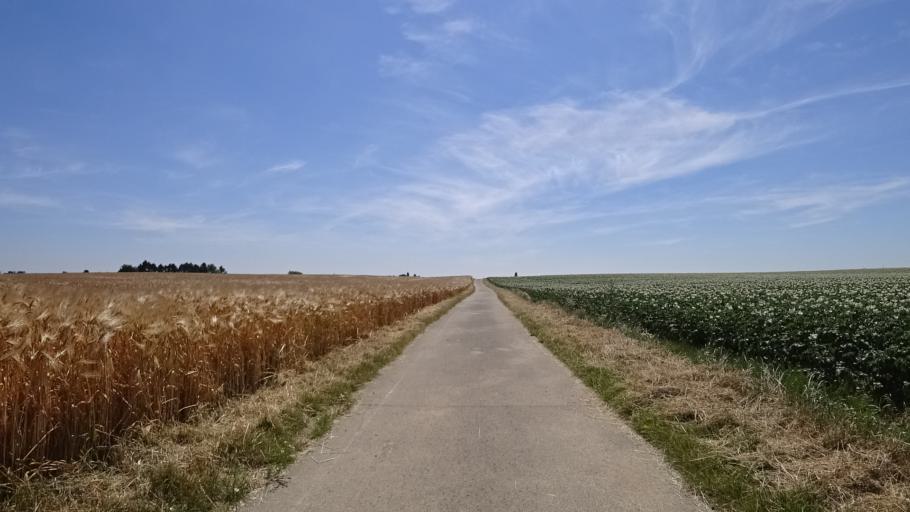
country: BE
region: Wallonia
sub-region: Province de Namur
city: Gembloux
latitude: 50.5743
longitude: 4.6793
